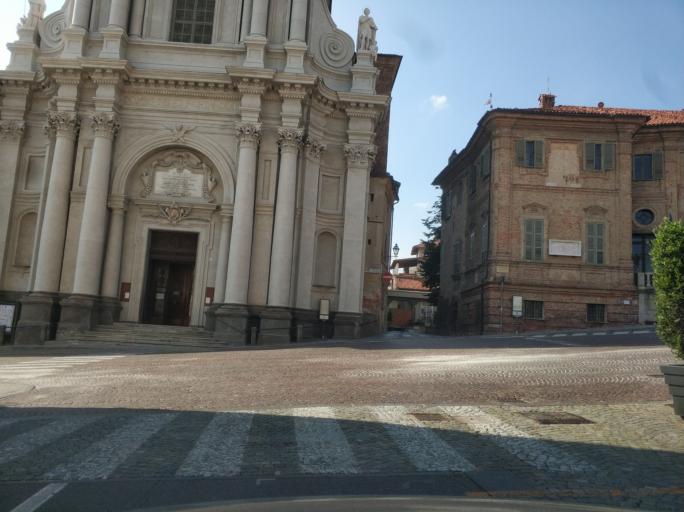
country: IT
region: Piedmont
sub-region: Provincia di Cuneo
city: Bra
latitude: 44.6978
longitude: 7.8547
